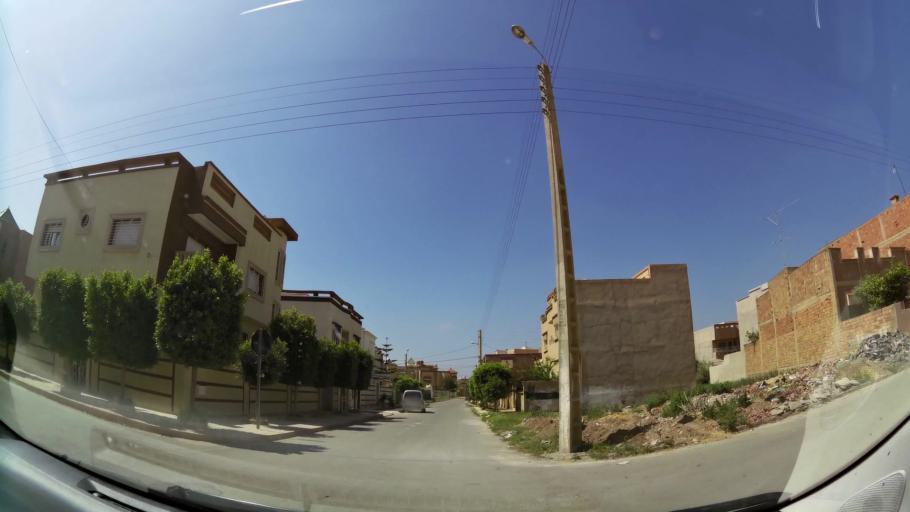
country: MA
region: Oriental
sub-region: Oujda-Angad
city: Oujda
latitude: 34.6860
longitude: -1.8768
